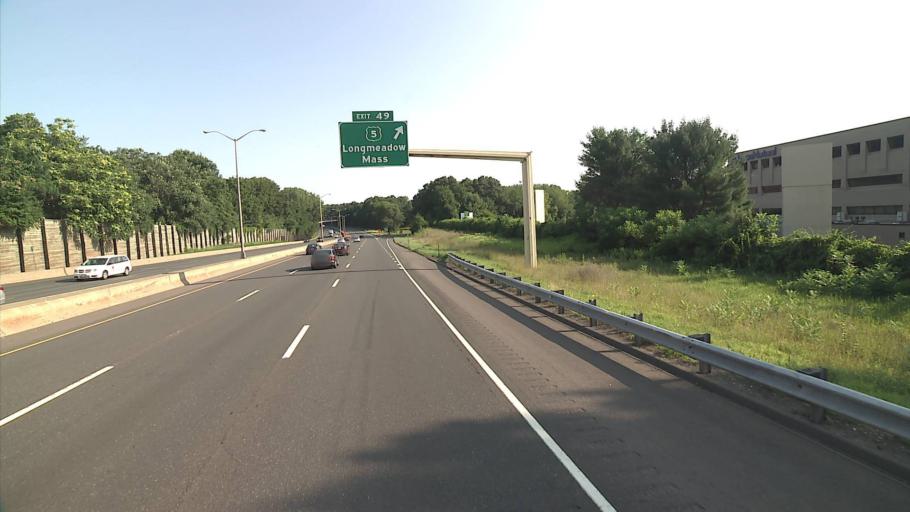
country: US
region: Connecticut
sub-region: Hartford County
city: Sherwood Manor
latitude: 42.0160
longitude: -72.5866
